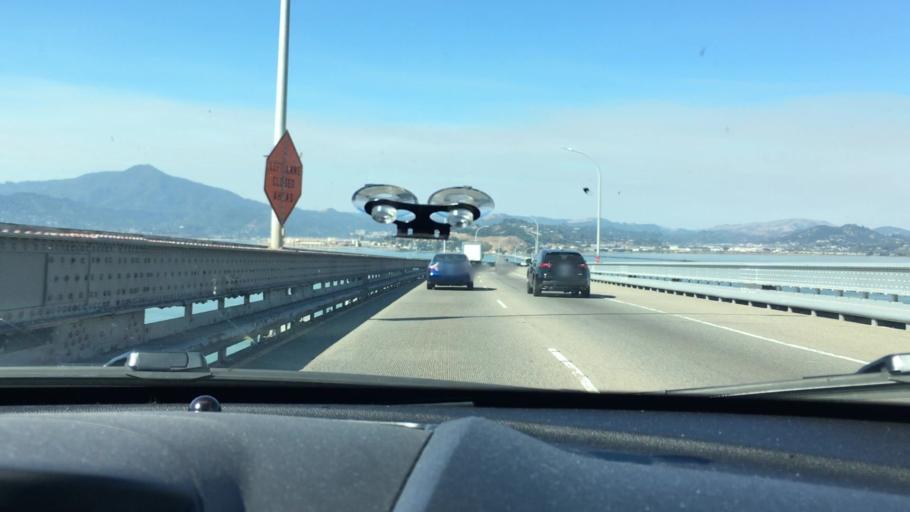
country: US
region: California
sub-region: Marin County
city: Tiburon
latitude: 37.9360
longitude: -122.4519
